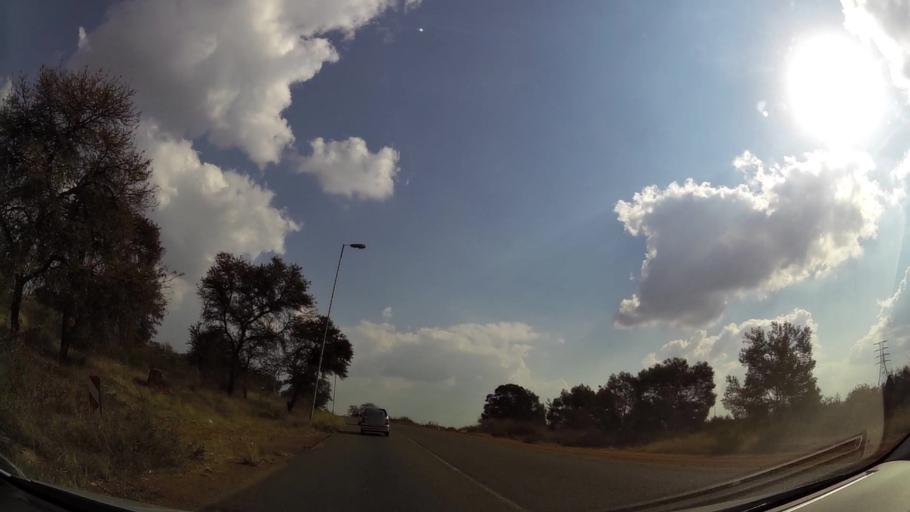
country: ZA
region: Gauteng
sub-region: City of Tshwane Metropolitan Municipality
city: Centurion
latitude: -25.8624
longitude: 28.2429
